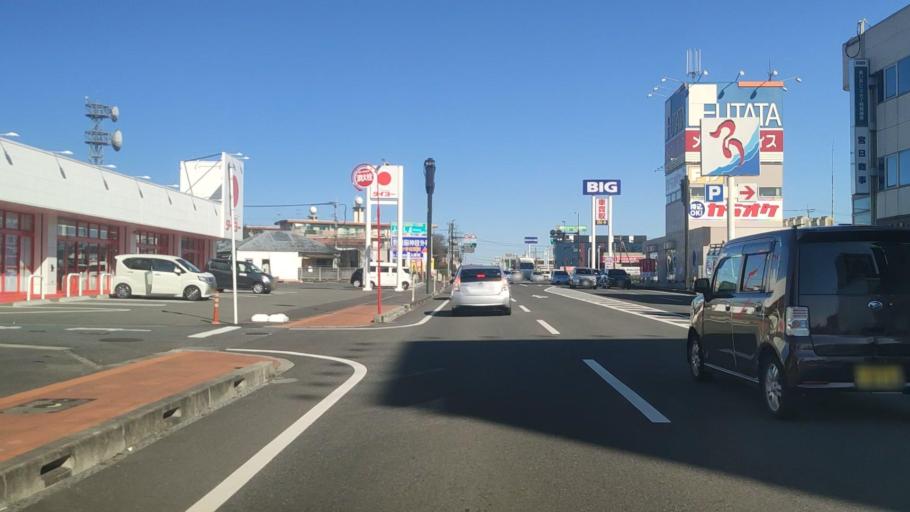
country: JP
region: Miyazaki
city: Miyakonojo
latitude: 31.7393
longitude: 131.0710
